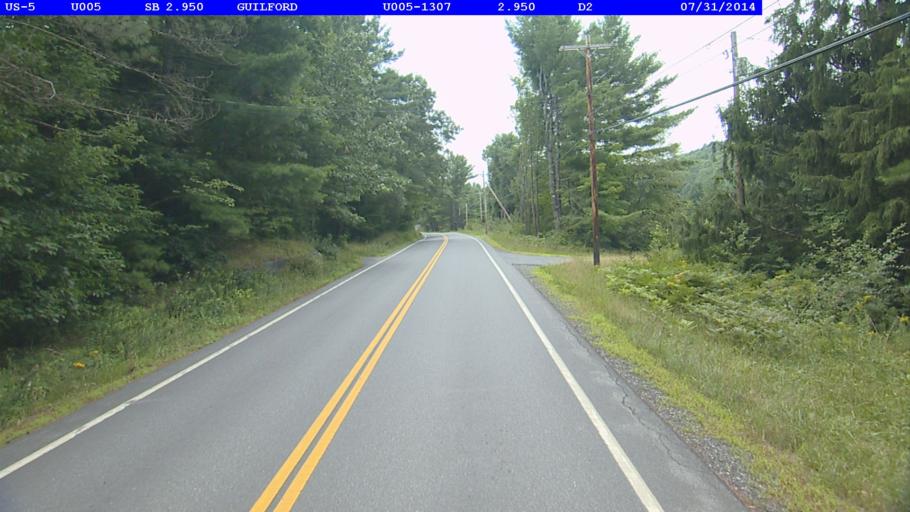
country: US
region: Vermont
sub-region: Windham County
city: Brattleboro
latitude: 42.7719
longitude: -72.5668
